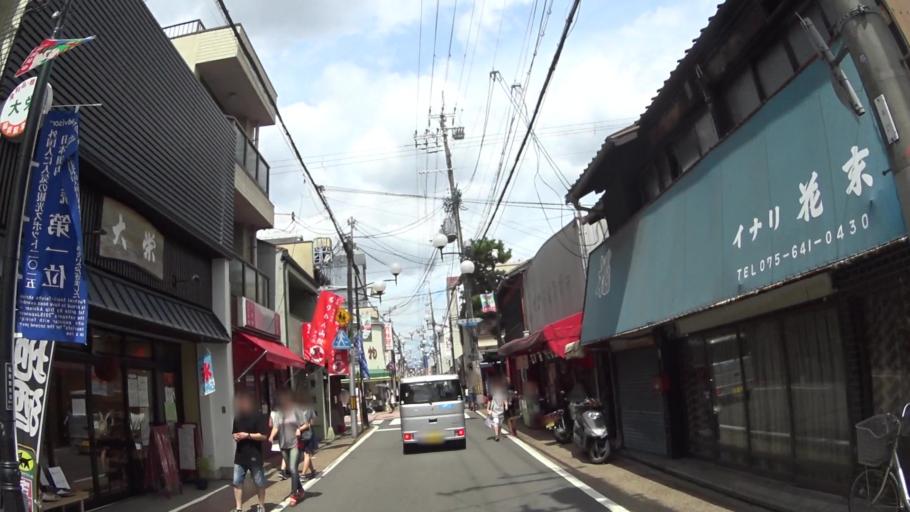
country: JP
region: Kyoto
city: Kyoto
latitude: 34.9675
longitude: 135.7709
